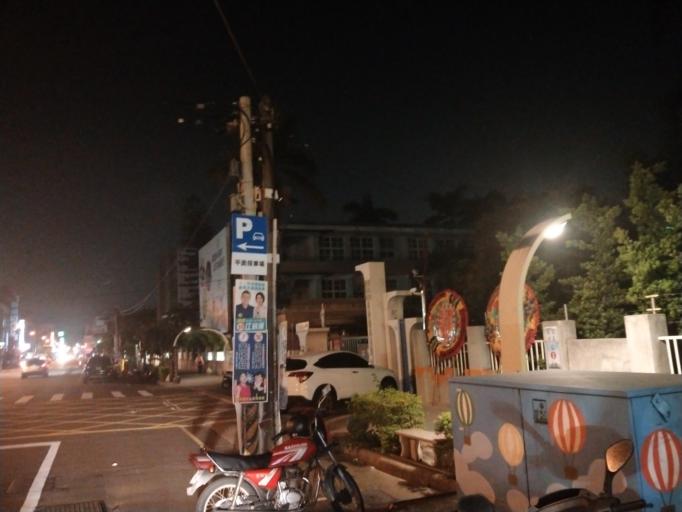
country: TW
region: Taiwan
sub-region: Changhua
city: Chang-hua
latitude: 24.0725
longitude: 120.5362
